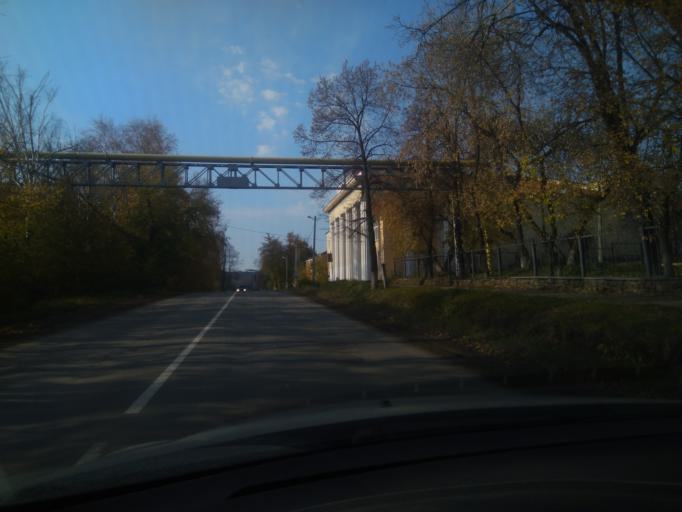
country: RU
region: Sverdlovsk
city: Nizhniye Sergi
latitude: 56.6682
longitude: 59.3179
